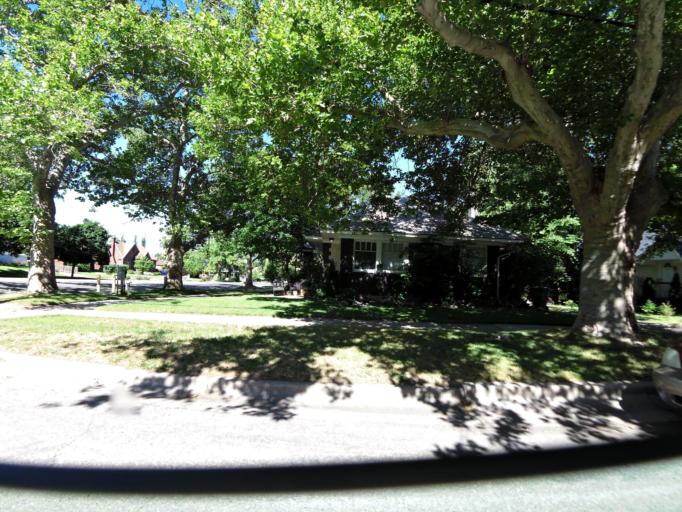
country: US
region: Utah
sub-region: Weber County
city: Ogden
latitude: 41.2205
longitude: -111.9455
